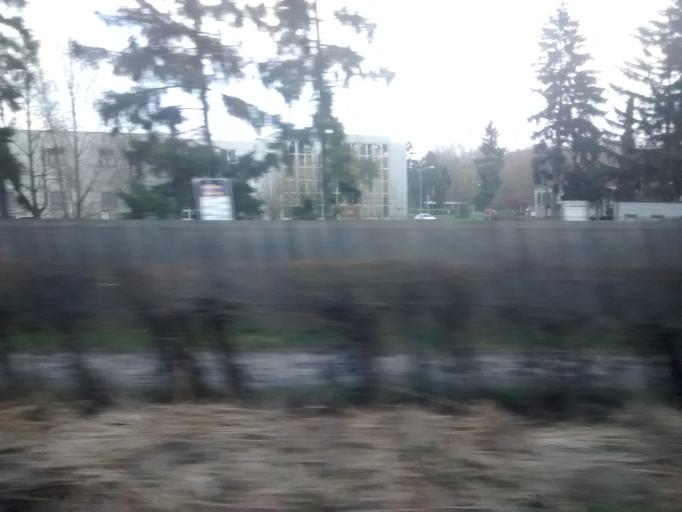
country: NL
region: Limburg
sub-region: Gemeente Schinnen
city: Puth
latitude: 50.9407
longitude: 5.8654
